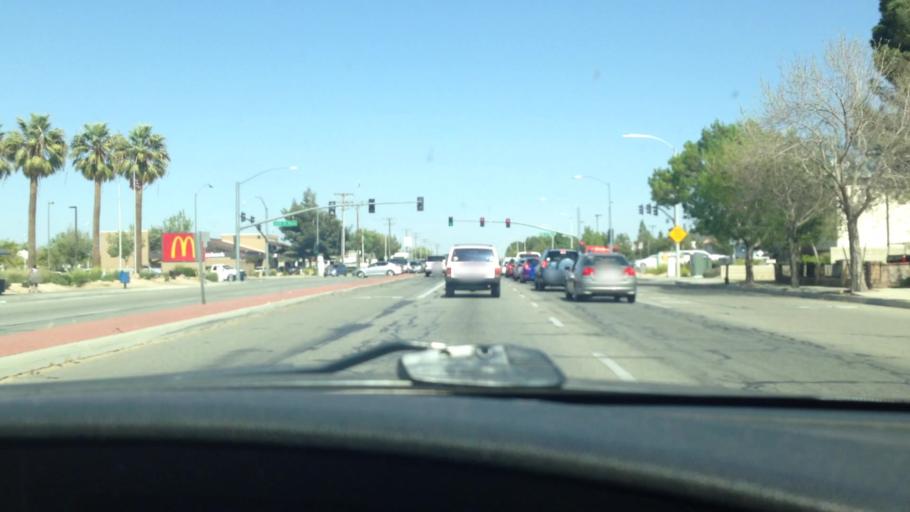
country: US
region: California
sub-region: Los Angeles County
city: Quartz Hill
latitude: 34.6603
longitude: -118.1847
